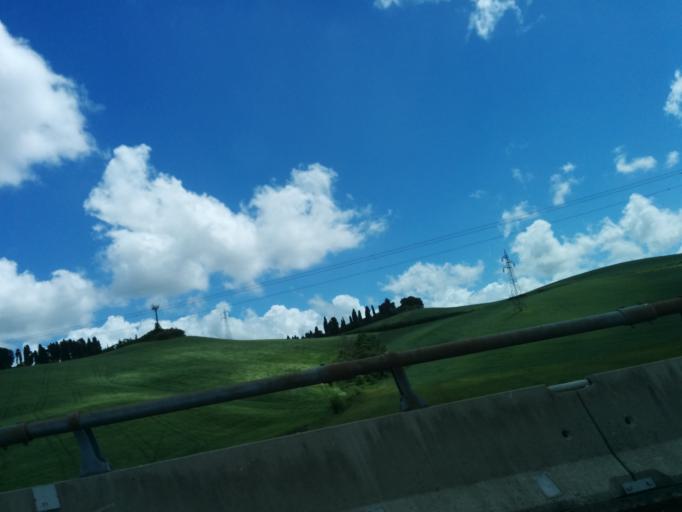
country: IT
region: Tuscany
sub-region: Provincia di Livorno
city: Collesalvetti
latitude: 43.5443
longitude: 10.4699
